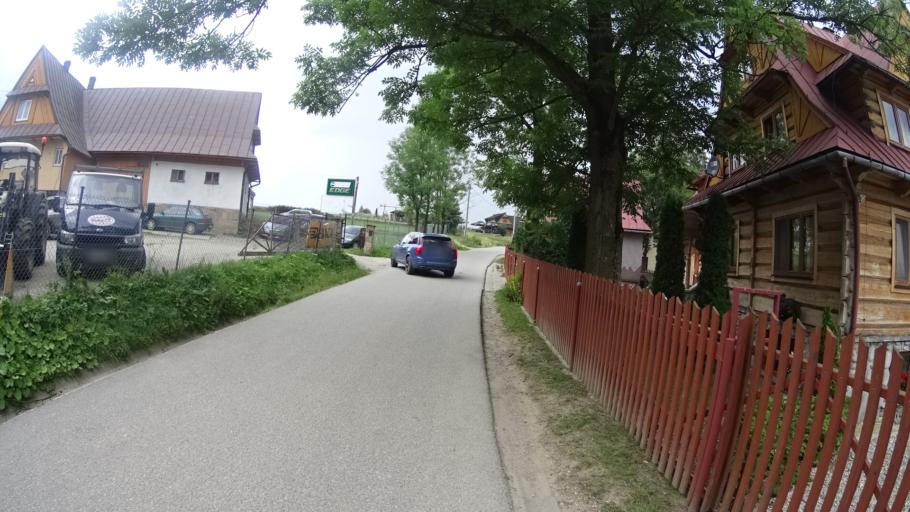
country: PL
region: Lesser Poland Voivodeship
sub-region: Powiat tatrzanski
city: Zakopane
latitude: 49.3216
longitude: 19.9556
